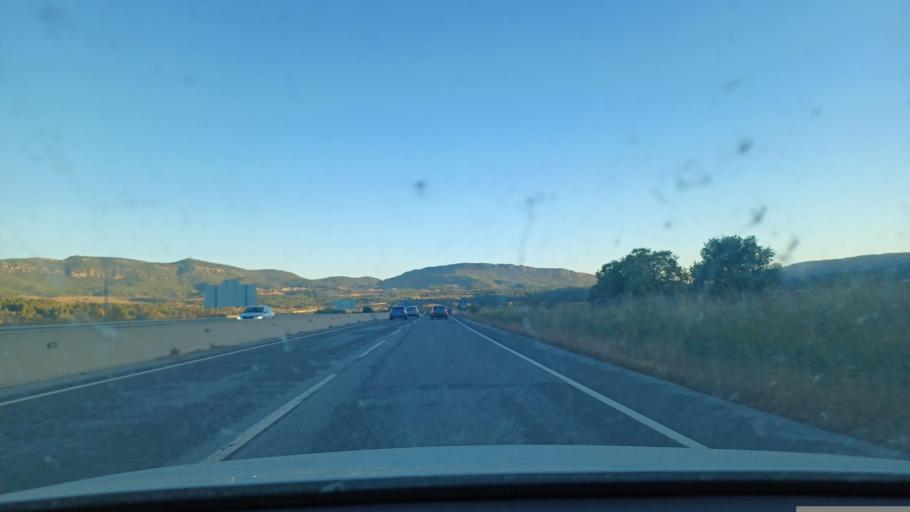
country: ES
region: Catalonia
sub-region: Provincia de Tarragona
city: Montblanc
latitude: 41.3813
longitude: 1.1705
